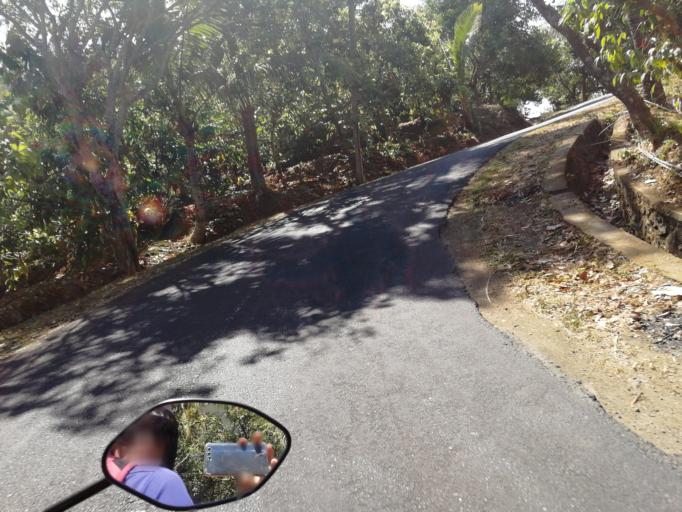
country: ID
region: Bali
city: Banjar Kedisan
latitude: -8.1435
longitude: 115.3148
